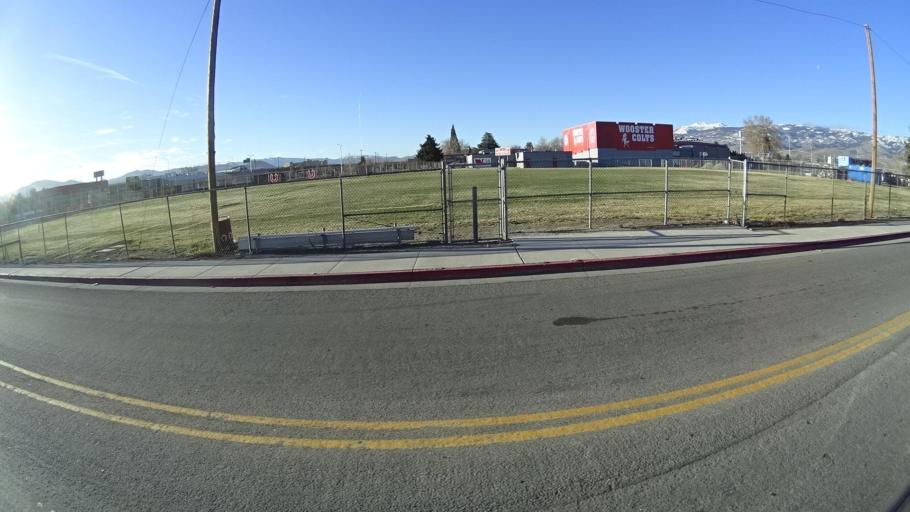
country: US
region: Nevada
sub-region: Washoe County
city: Reno
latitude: 39.5095
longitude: -119.7818
